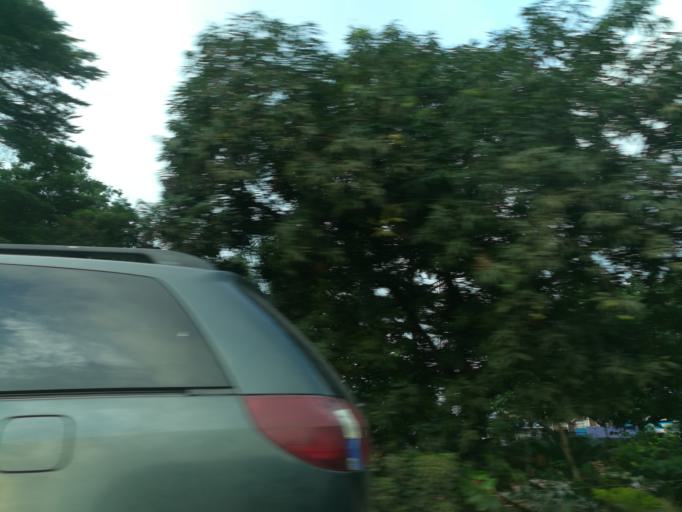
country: NG
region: Lagos
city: Ojota
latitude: 6.6080
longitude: 3.3719
